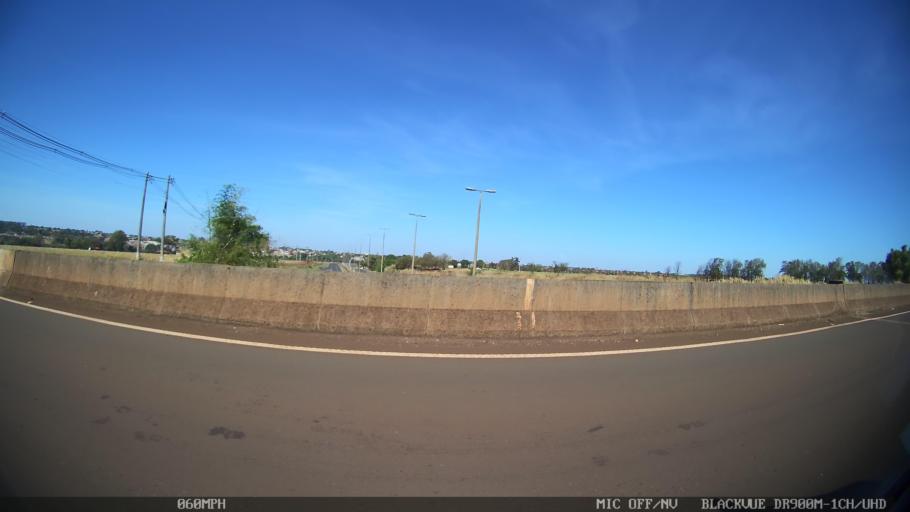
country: BR
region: Sao Paulo
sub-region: Barretos
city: Barretos
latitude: -20.5274
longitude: -48.5910
